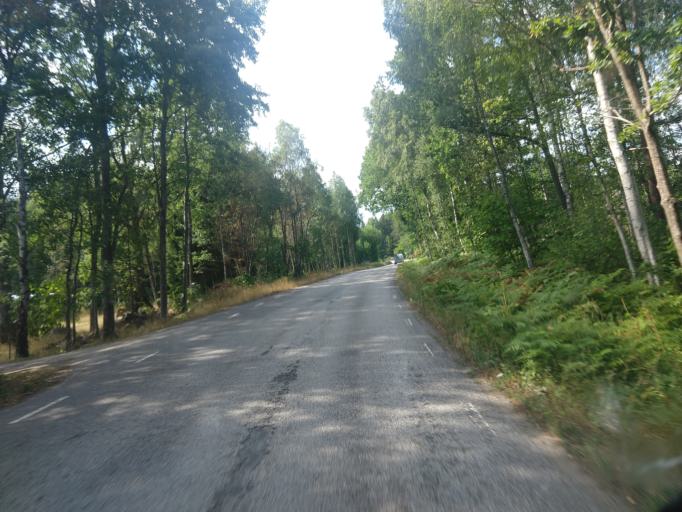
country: SE
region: Blekinge
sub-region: Karlskrona Kommun
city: Rodeby
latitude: 56.2404
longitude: 15.5643
